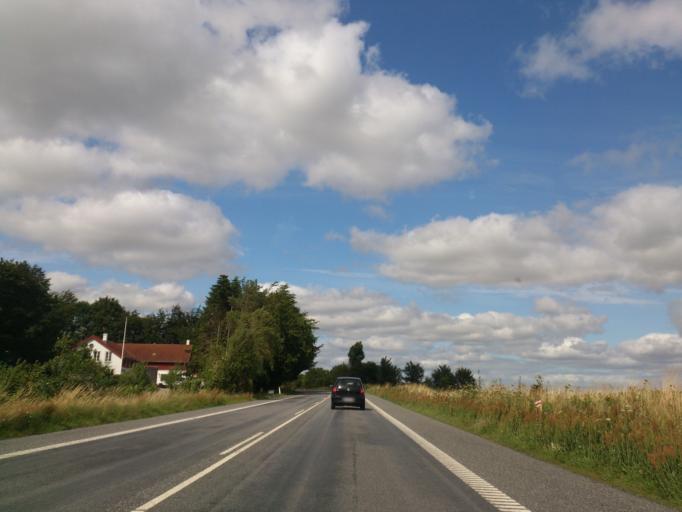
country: DK
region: South Denmark
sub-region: Aabenraa Kommune
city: Krusa
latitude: 54.9070
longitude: 9.4398
